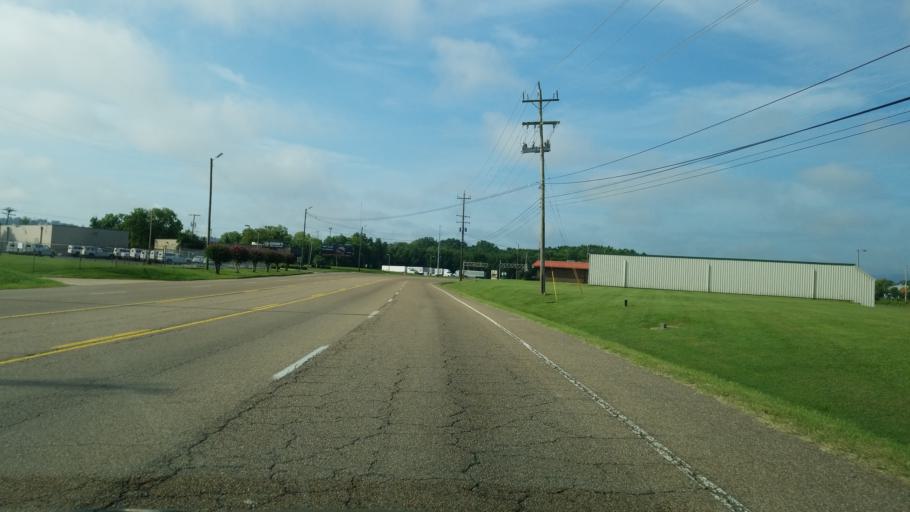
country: US
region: Tennessee
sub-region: Hamilton County
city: East Chattanooga
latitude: 35.0622
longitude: -85.2742
